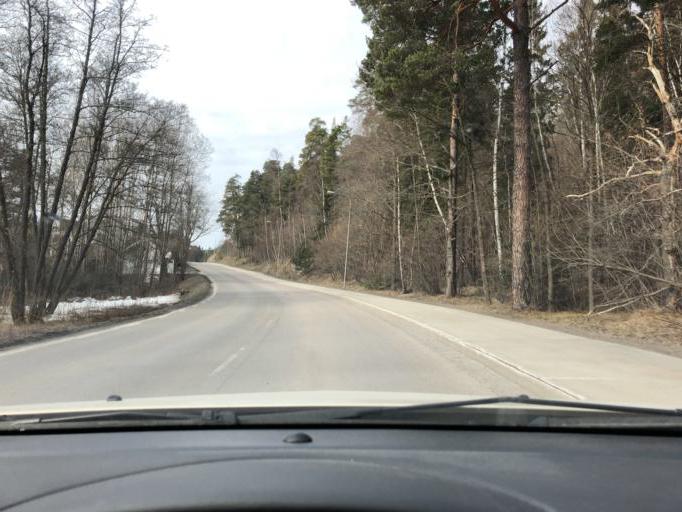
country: SE
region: Stockholm
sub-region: Nacka Kommun
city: Boo
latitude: 59.3334
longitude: 18.3079
